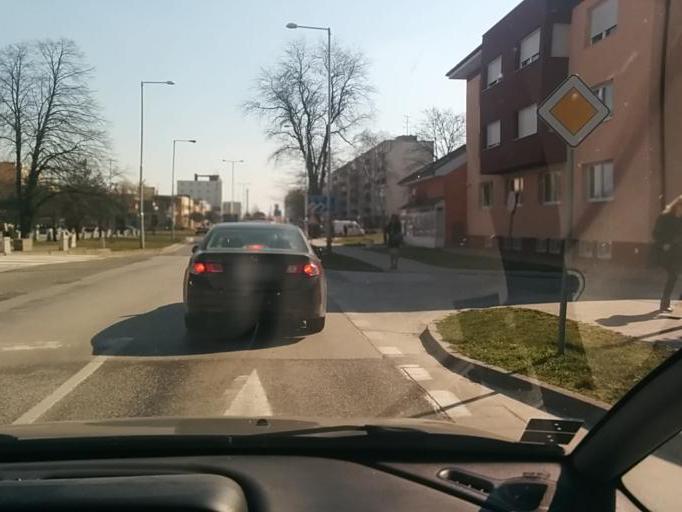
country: SK
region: Trnavsky
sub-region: Okres Galanta
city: Galanta
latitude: 48.1900
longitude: 17.7250
